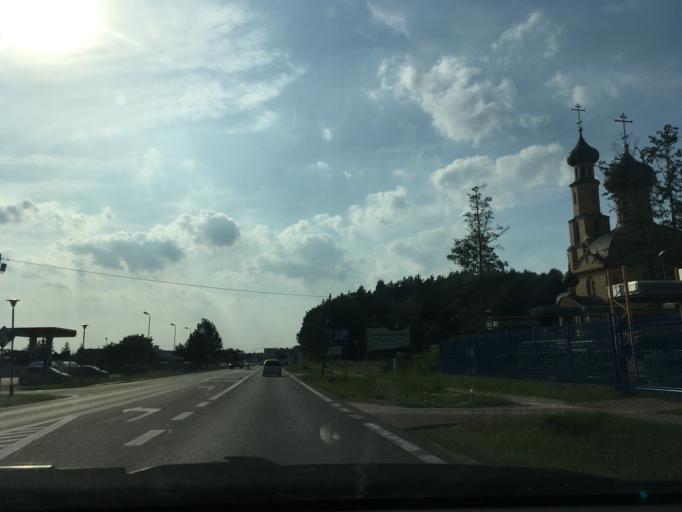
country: PL
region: Podlasie
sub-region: Bialystok
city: Bialystok
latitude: 53.1257
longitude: 23.2411
